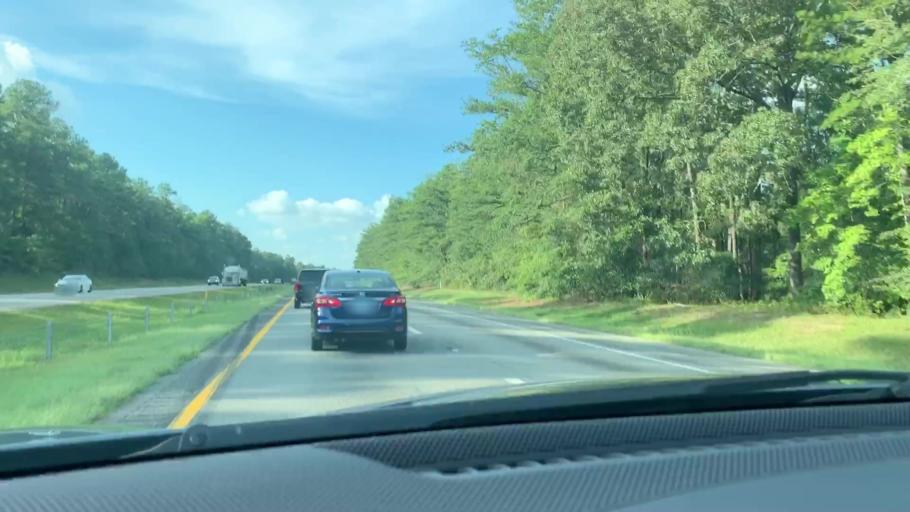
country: US
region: South Carolina
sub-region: Orangeburg County
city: Brookdale
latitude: 33.5994
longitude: -80.8585
